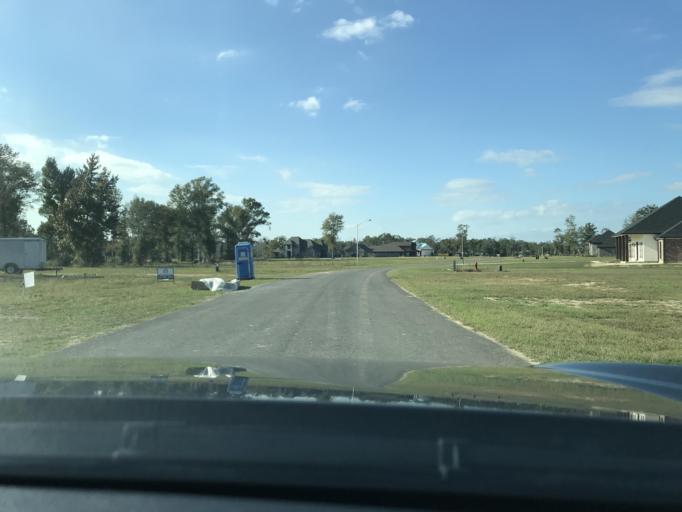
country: US
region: Louisiana
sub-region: Calcasieu Parish
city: Moss Bluff
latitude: 30.3339
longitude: -93.2488
